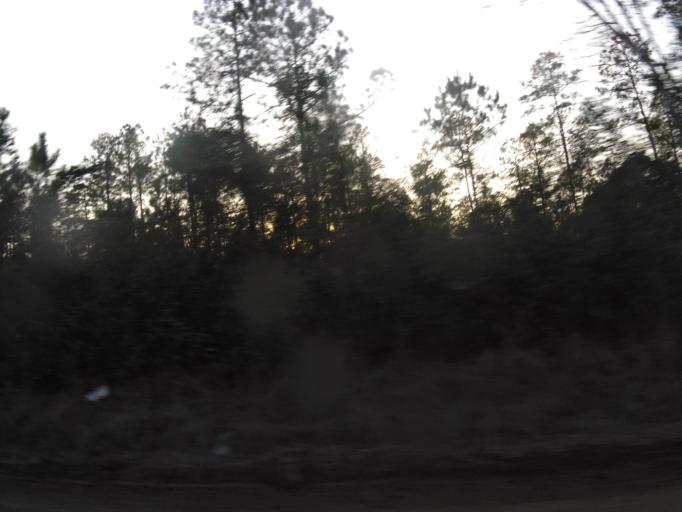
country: US
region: Florida
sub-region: Clay County
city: Green Cove Springs
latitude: 29.8462
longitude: -81.7971
